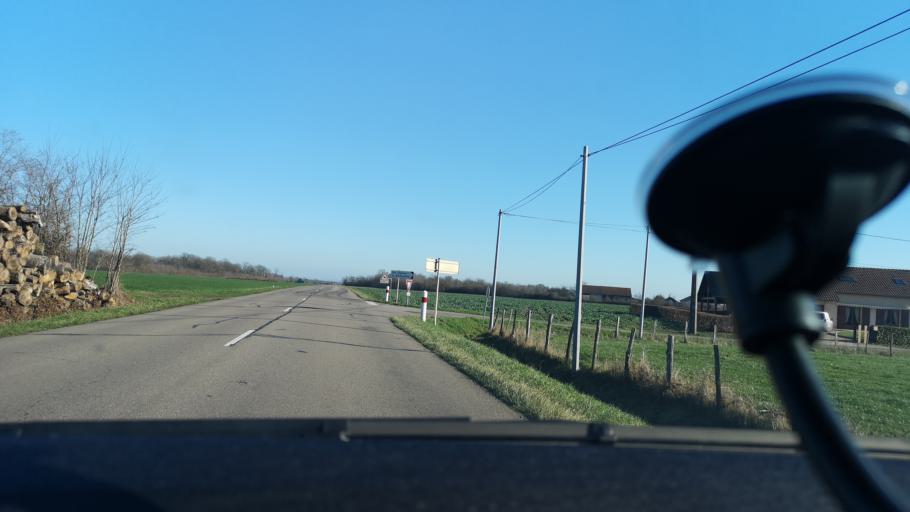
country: FR
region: Bourgogne
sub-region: Departement de Saone-et-Loire
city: Mervans
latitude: 46.7447
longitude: 5.1371
